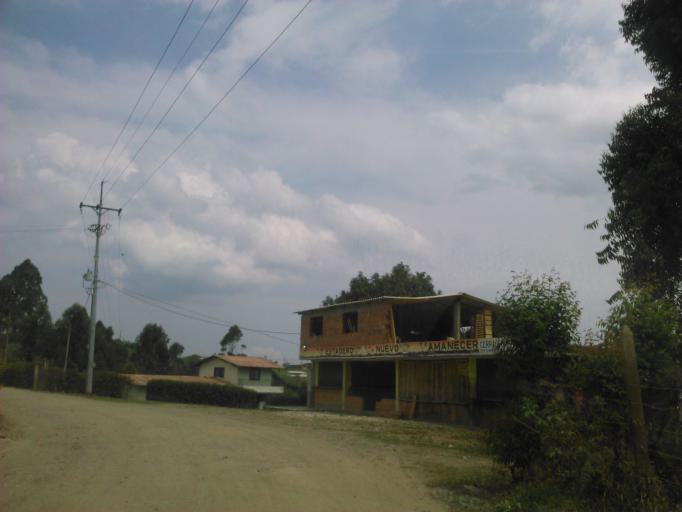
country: CO
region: Antioquia
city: San Vicente
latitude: 6.2522
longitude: -75.3675
